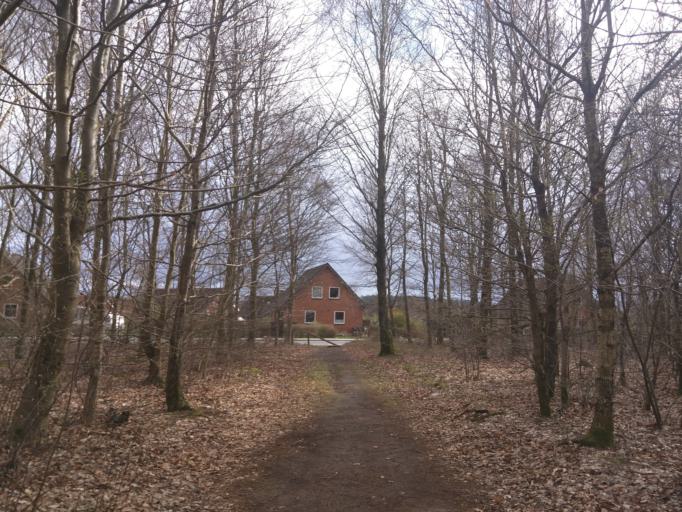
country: DK
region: Central Jutland
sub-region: Silkeborg Kommune
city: Silkeborg
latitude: 56.1779
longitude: 9.5288
